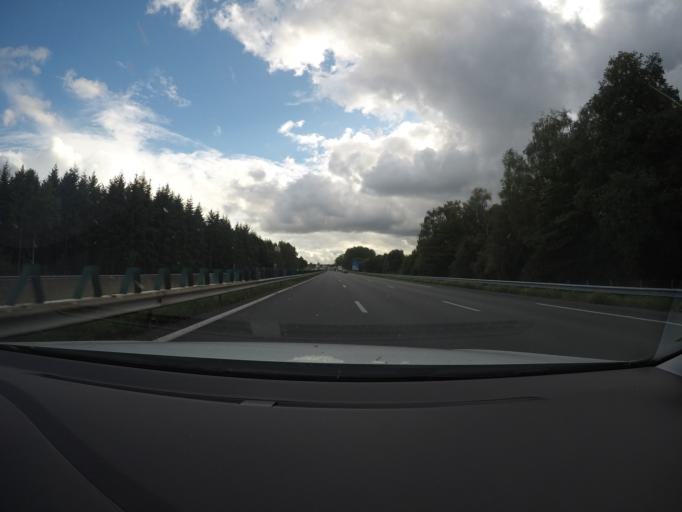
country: FR
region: Picardie
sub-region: Departement de l'Oise
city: Ressons-sur-Matz
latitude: 49.5333
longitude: 2.7244
